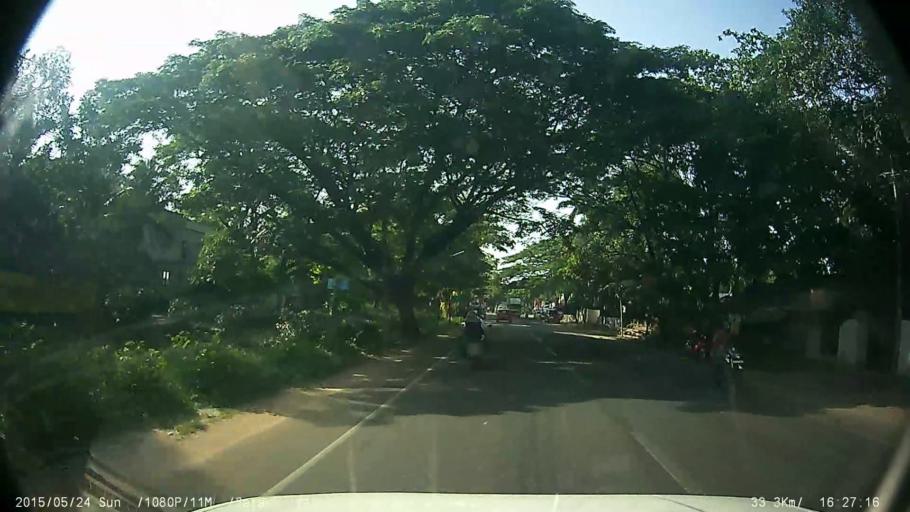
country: IN
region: Kerala
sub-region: Alappuzha
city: Alleppey
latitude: 9.5272
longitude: 76.3275
